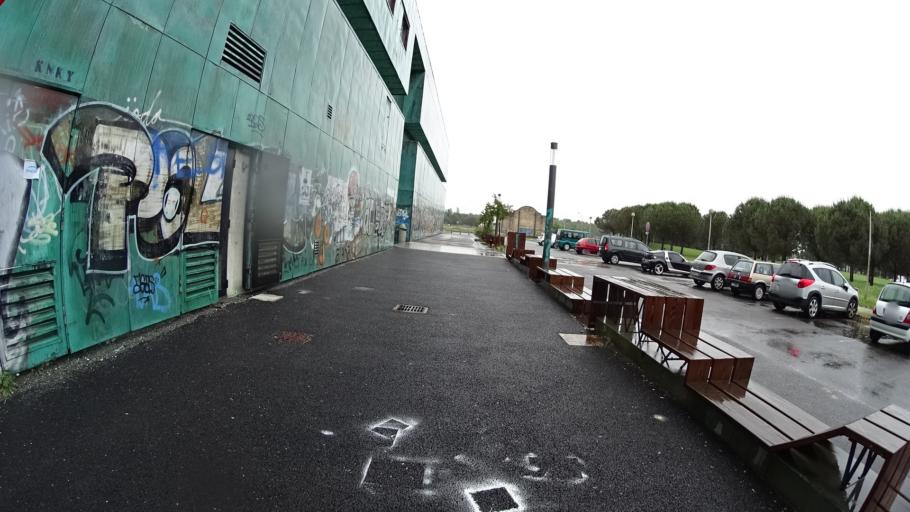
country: FR
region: Aquitaine
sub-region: Departement de la Gironde
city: Gradignan
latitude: 44.7946
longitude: -0.6161
